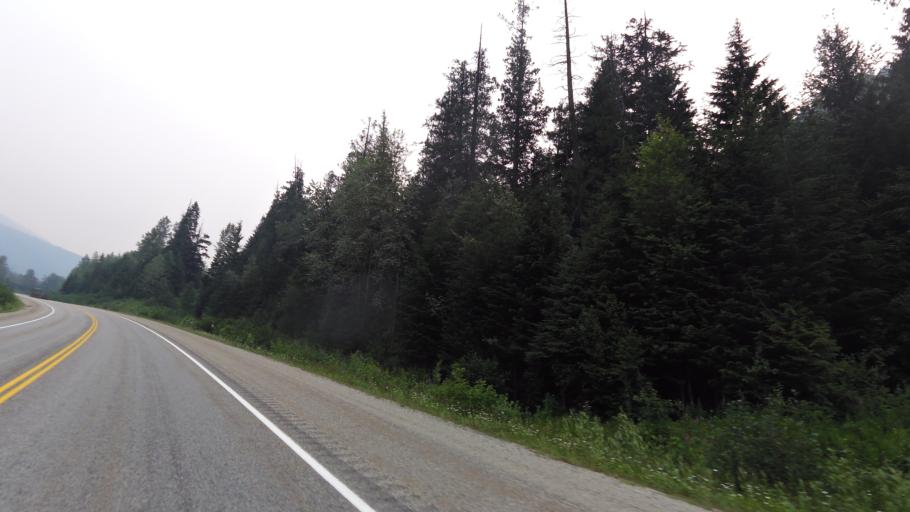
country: CA
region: Alberta
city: Jasper Park Lodge
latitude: 52.3326
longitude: -119.1783
